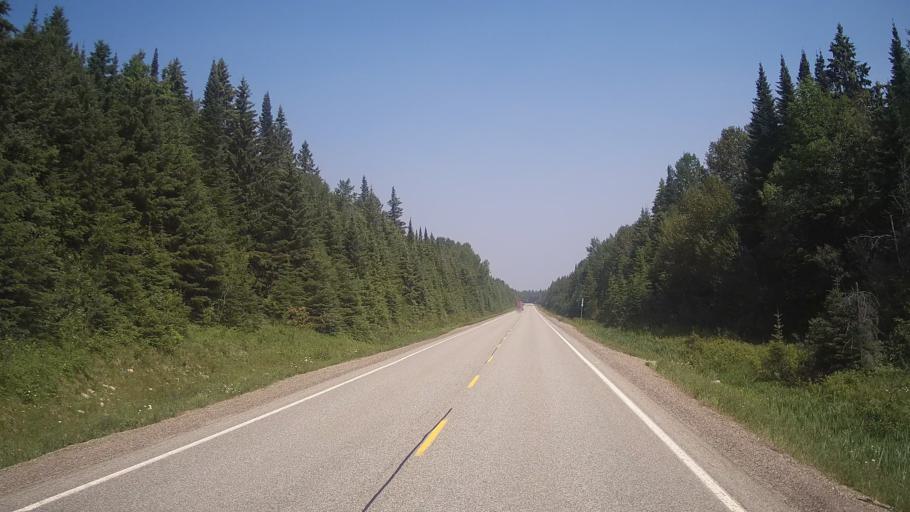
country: CA
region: Ontario
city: Timmins
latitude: 48.2068
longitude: -81.5764
